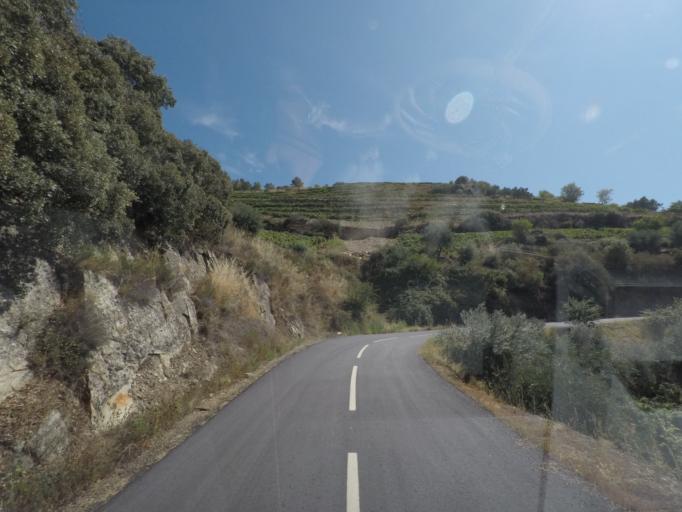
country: PT
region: Vila Real
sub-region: Sabrosa
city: Sabrosa
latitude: 41.2217
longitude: -7.5256
